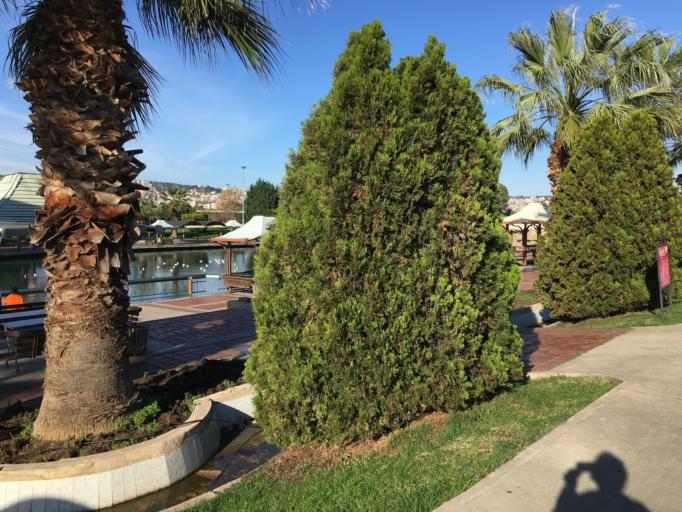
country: TR
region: Samsun
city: Samsun
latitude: 41.2860
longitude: 36.3454
